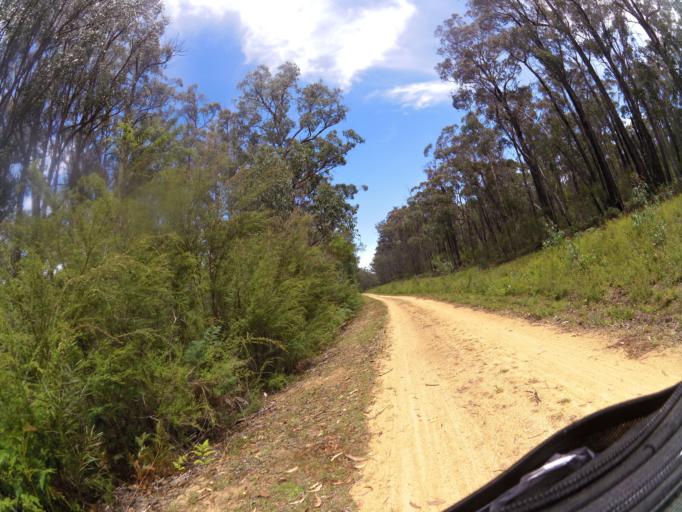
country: AU
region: Victoria
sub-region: East Gippsland
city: Lakes Entrance
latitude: -37.7408
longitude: 148.0040
